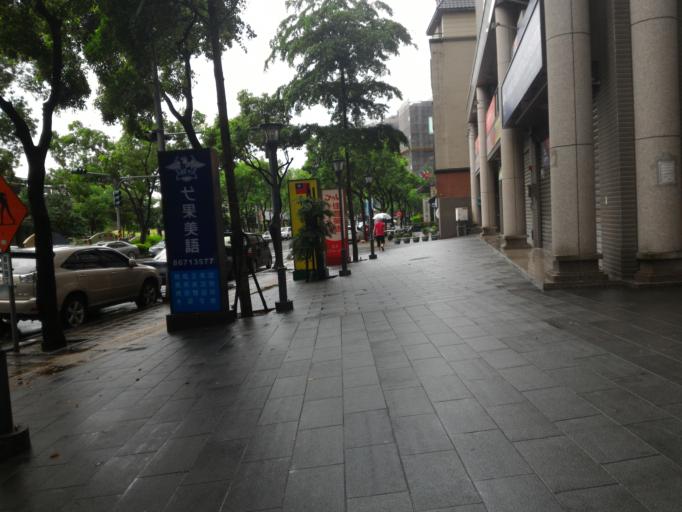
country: TW
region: Taiwan
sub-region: Taoyuan
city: Taoyuan
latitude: 24.9417
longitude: 121.3761
